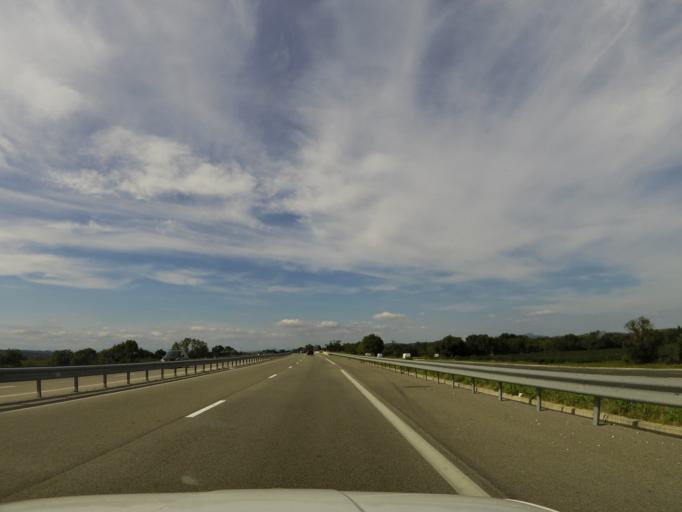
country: FR
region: Languedoc-Roussillon
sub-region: Departement du Gard
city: La Calmette
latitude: 43.9391
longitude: 4.2536
